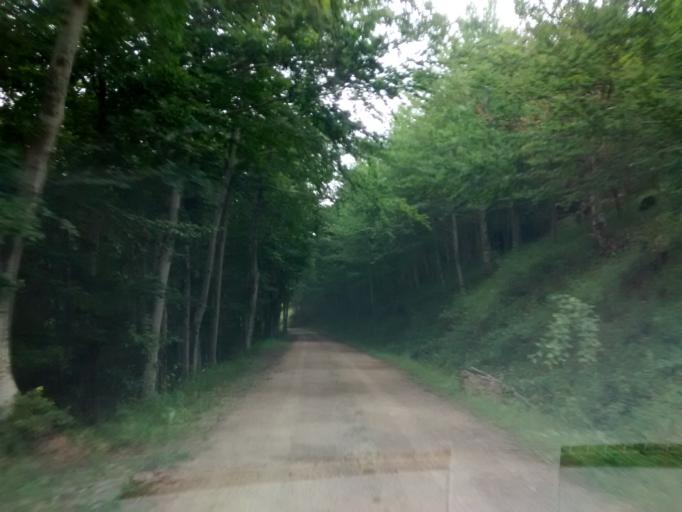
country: ES
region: La Rioja
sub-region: Provincia de La Rioja
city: Ajamil
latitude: 42.1386
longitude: -2.4816
